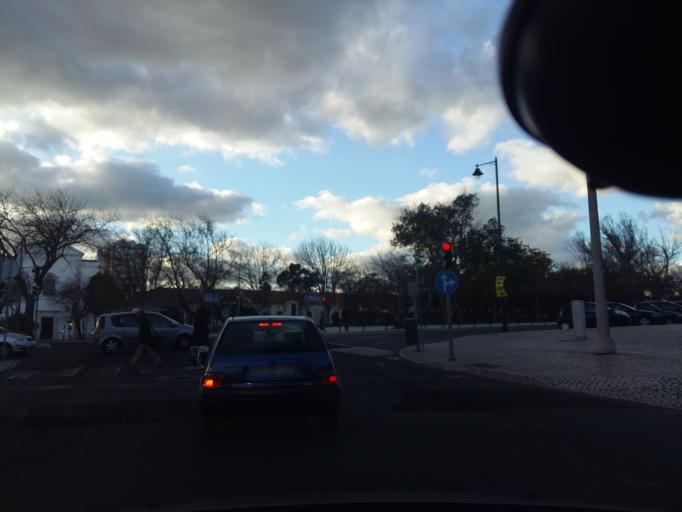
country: PT
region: Lisbon
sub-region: Odivelas
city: Pontinha
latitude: 38.7604
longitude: -9.1830
